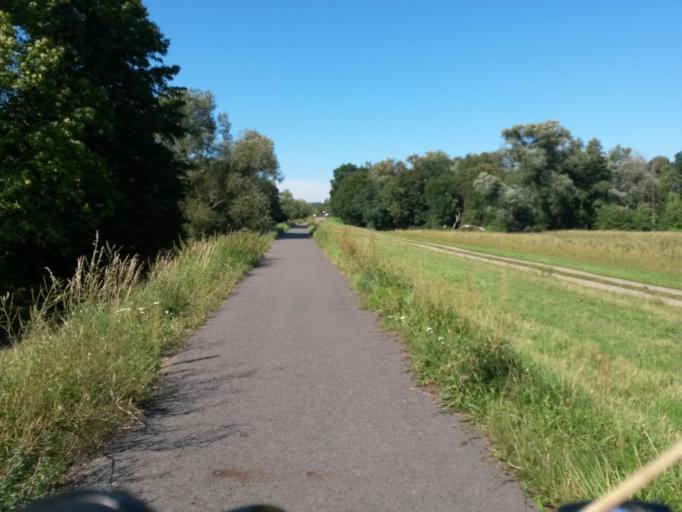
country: DE
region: Brandenburg
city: Schoneberg
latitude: 52.9474
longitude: 14.1111
